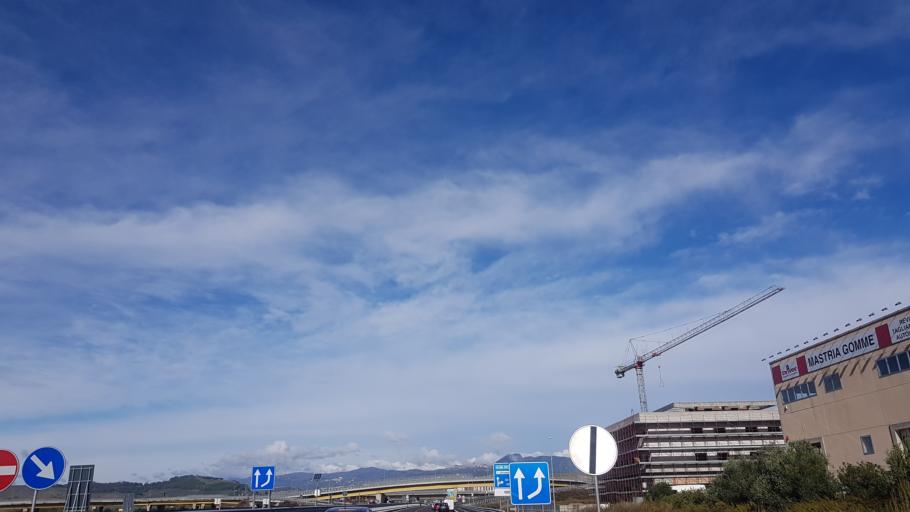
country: IT
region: Calabria
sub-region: Provincia di Catanzaro
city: Roccelletta
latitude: 38.8474
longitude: 16.5812
